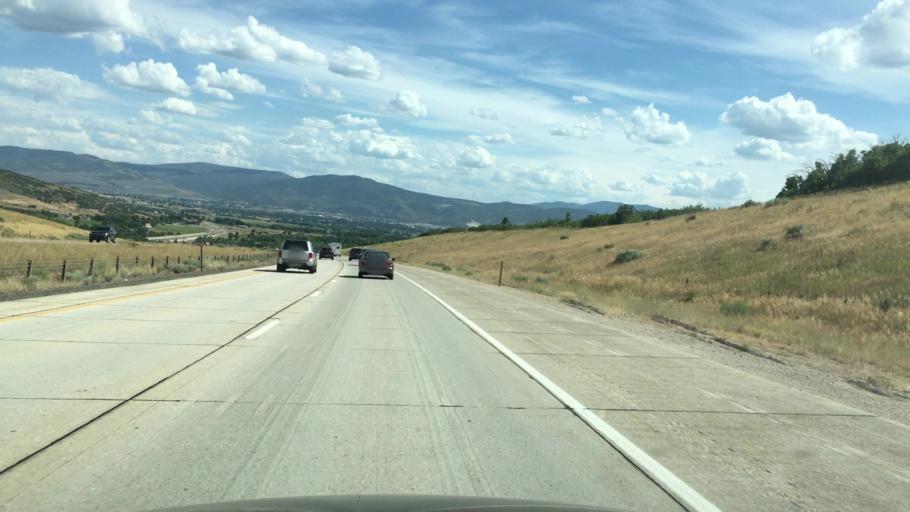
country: US
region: Utah
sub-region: Wasatch County
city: Heber
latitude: 40.5790
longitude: -111.4362
